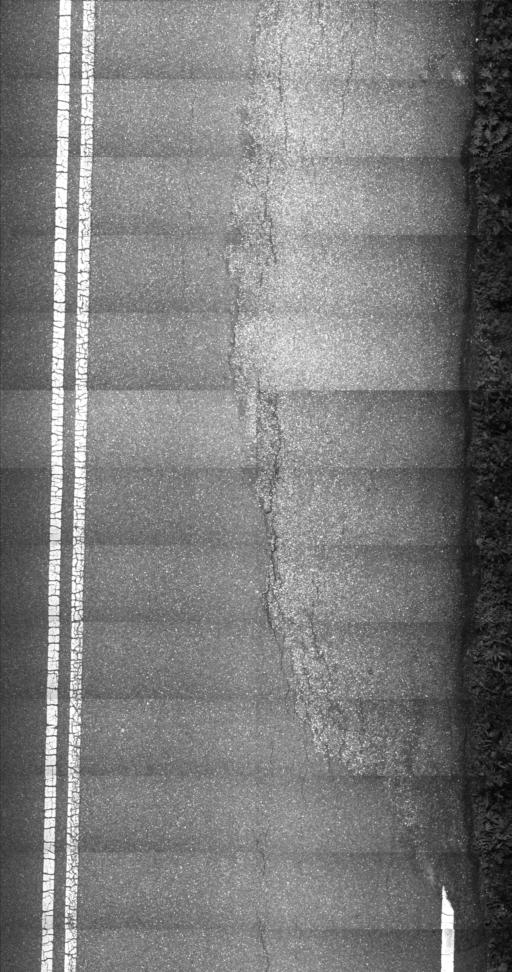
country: US
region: Vermont
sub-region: Lamoille County
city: Johnson
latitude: 44.5635
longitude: -72.7855
